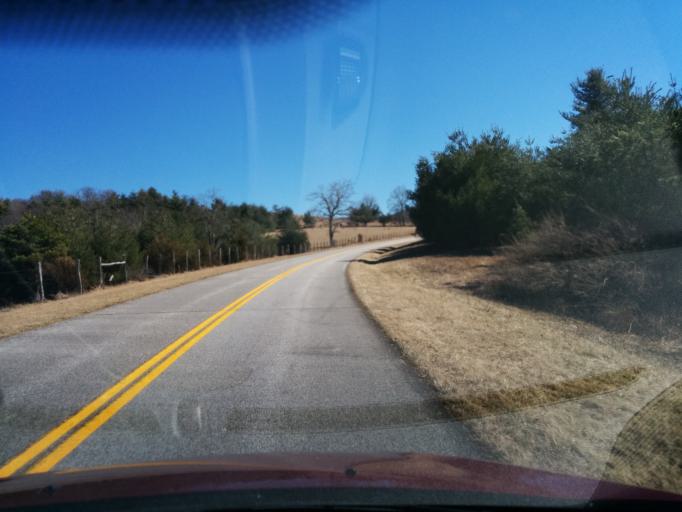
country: US
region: Virginia
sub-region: Augusta County
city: Stuarts Draft
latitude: 37.8609
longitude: -79.1459
